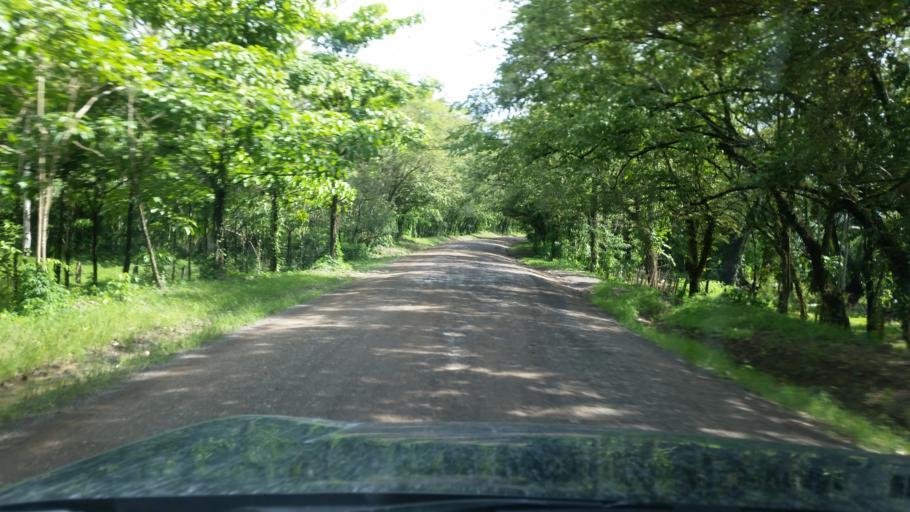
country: NI
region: Atlantico Norte (RAAN)
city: Siuna
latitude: 13.6964
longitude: -84.7836
